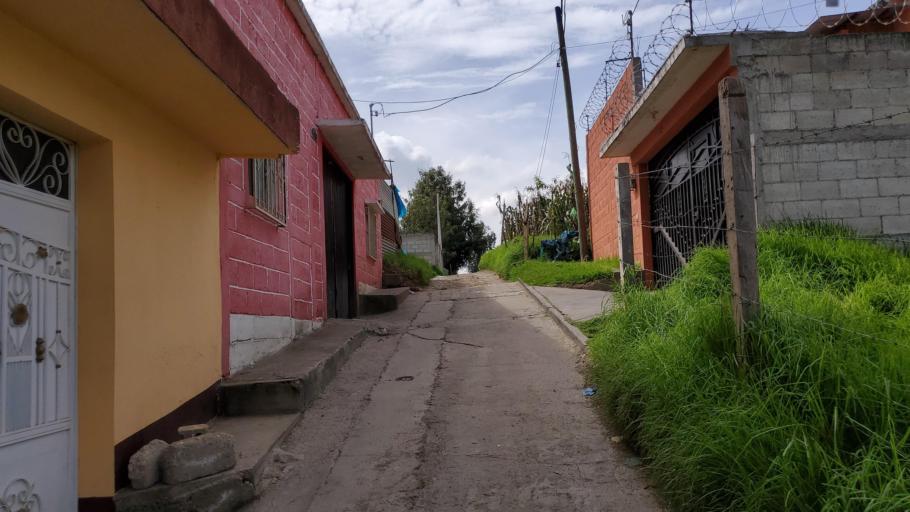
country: GT
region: Quetzaltenango
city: Quetzaltenango
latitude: 14.8396
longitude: -91.5381
